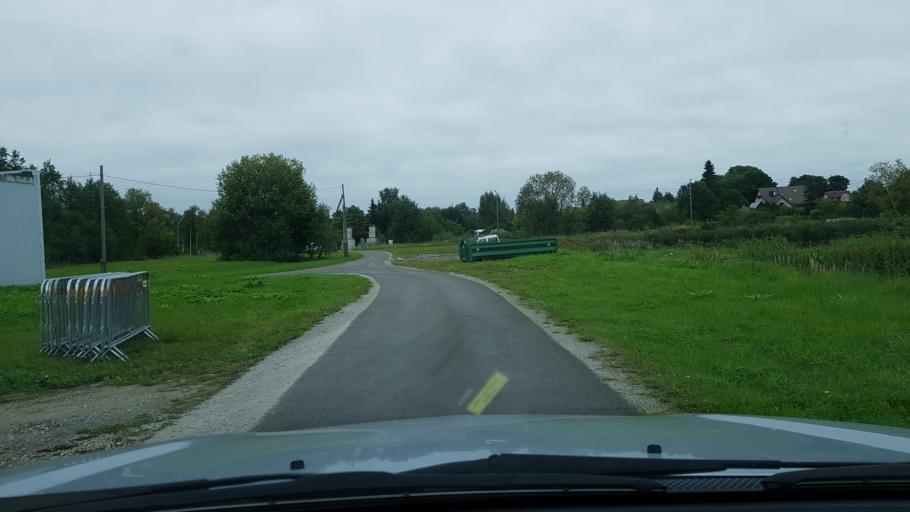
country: EE
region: Harju
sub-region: Rae vald
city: Jueri
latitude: 59.3526
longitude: 24.9183
